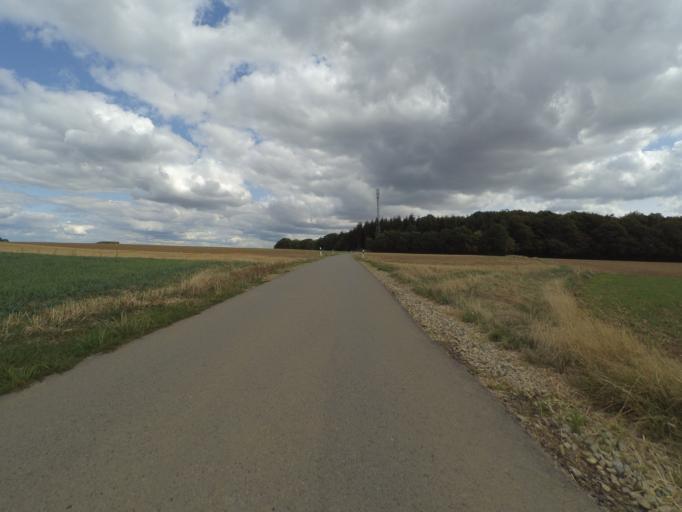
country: LU
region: Grevenmacher
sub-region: Canton de Remich
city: Dalheim
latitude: 49.5378
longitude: 6.2695
